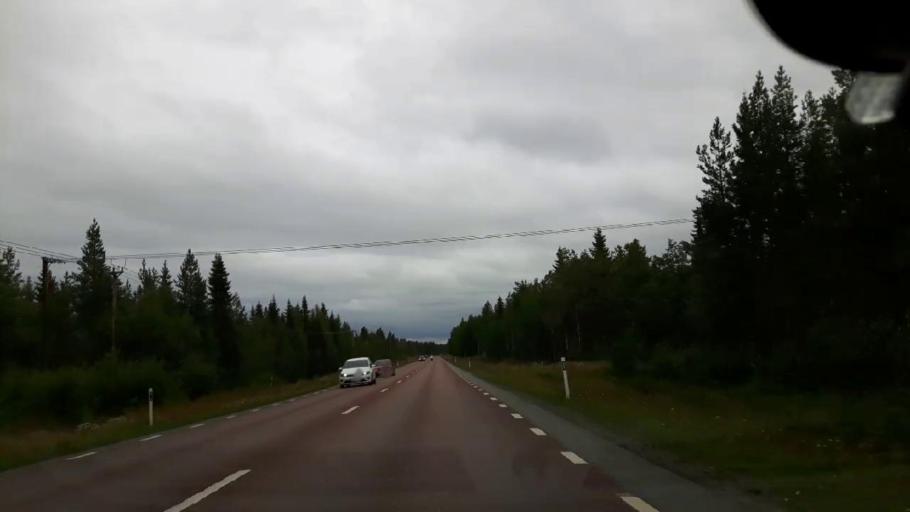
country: SE
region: Jaemtland
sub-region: Bergs Kommun
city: Hoverberg
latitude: 62.8551
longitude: 14.5180
